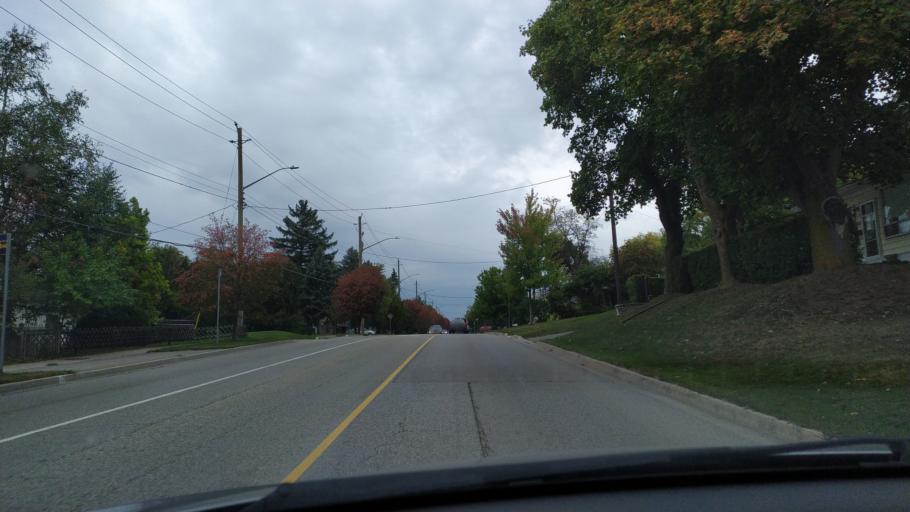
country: CA
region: Ontario
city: Waterloo
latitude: 43.4853
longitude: -80.4884
